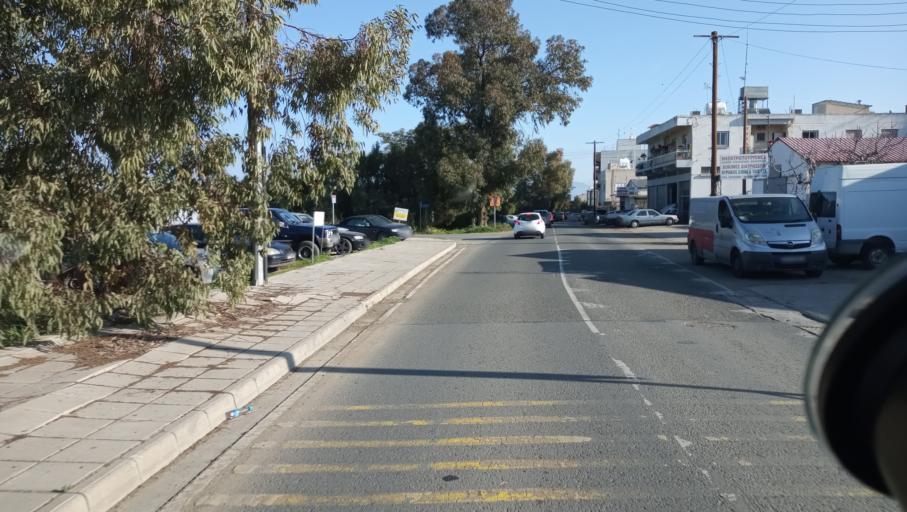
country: CY
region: Lefkosia
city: Nicosia
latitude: 35.1316
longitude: 33.3258
